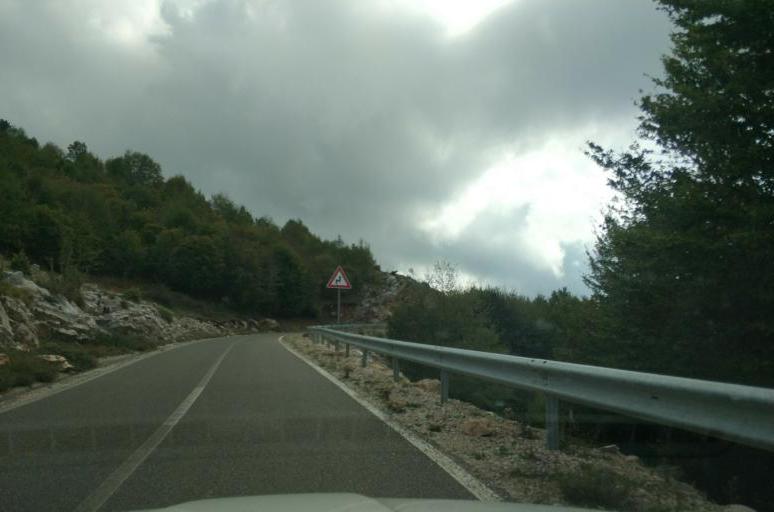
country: AL
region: Durres
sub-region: Rrethi i Krujes
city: Kruje
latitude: 41.5206
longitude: 19.8055
